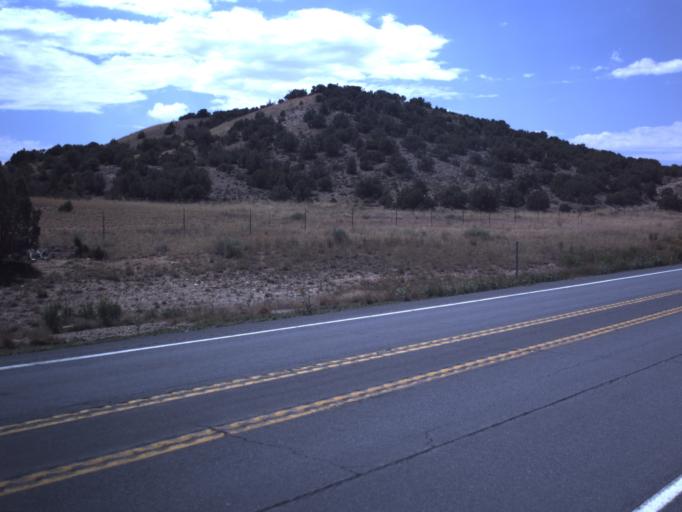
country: US
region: Utah
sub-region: Duchesne County
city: Duchesne
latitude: 40.1719
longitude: -110.3395
